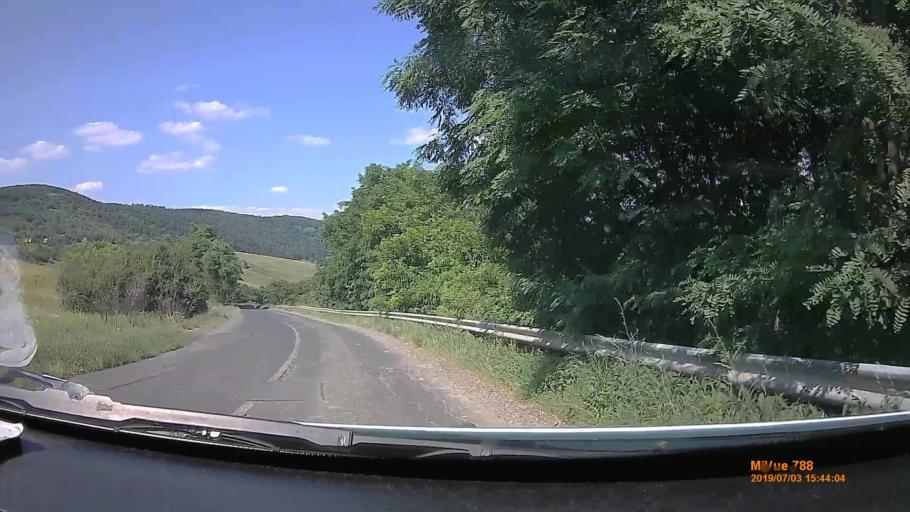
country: HU
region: Heves
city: Szilvasvarad
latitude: 48.1728
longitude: 20.4439
